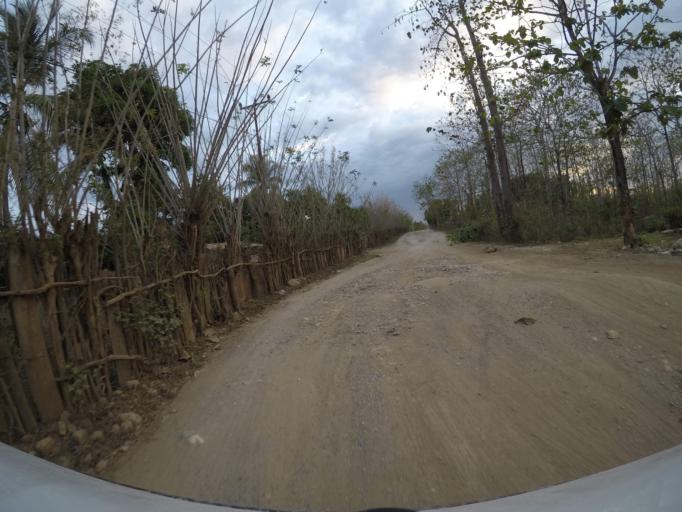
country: TL
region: Bobonaro
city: Maliana
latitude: -8.9243
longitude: 125.2082
